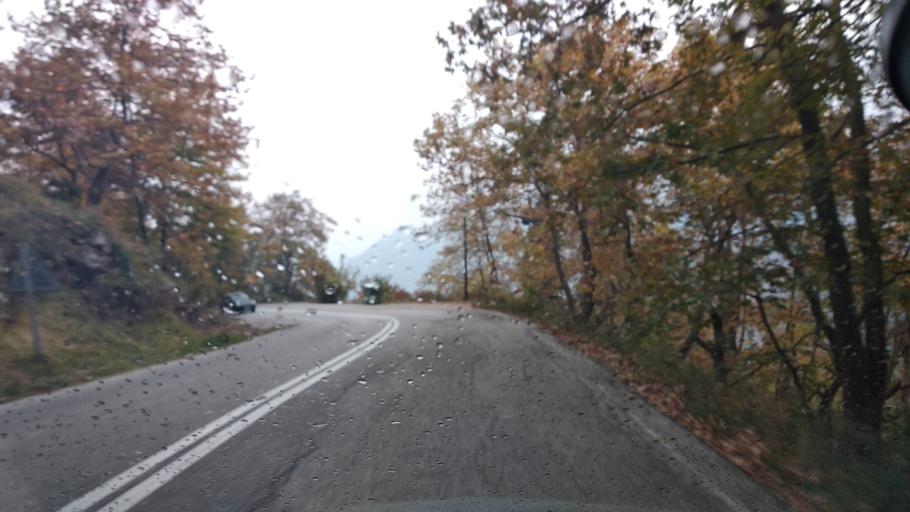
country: GR
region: Thessaly
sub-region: Trikala
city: Pyli
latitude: 39.5182
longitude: 21.5248
